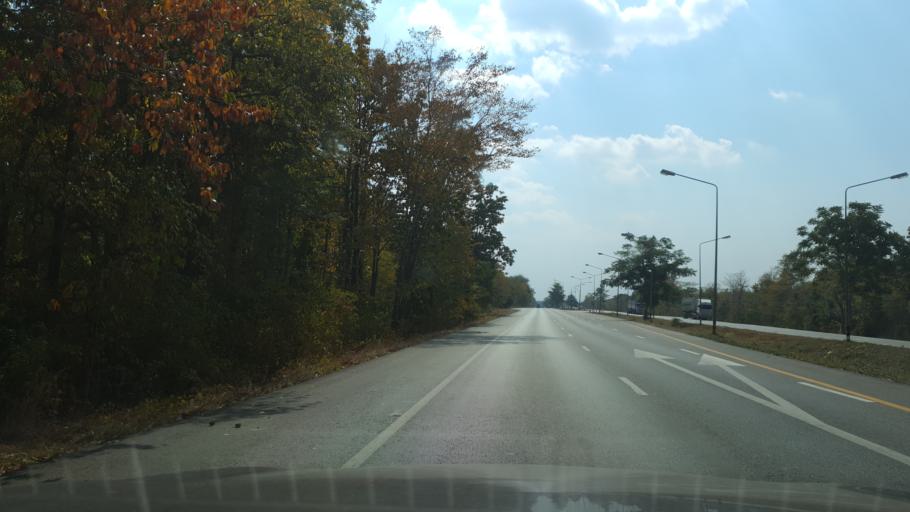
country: TH
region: Lampang
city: Mae Phrik
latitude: 17.3255
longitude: 99.1527
